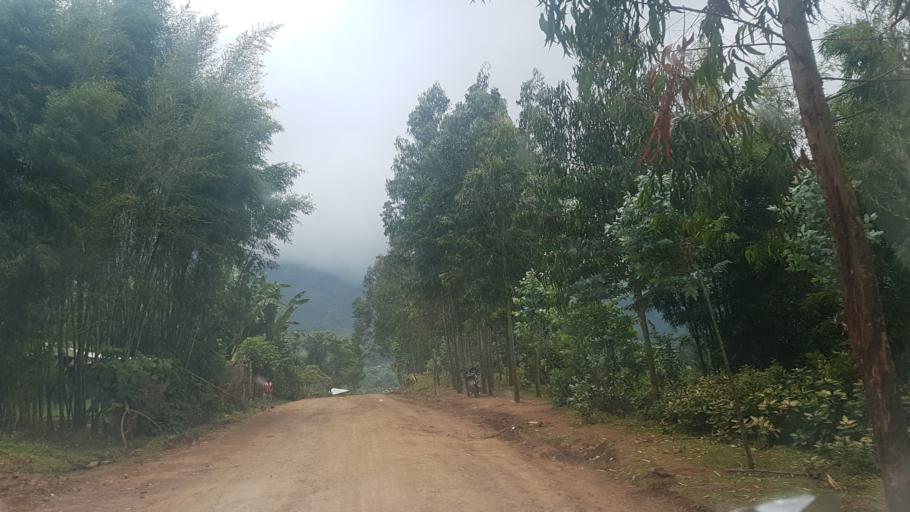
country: ET
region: Southern Nations, Nationalities, and People's Region
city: Arba Minch'
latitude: 6.3212
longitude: 37.5362
